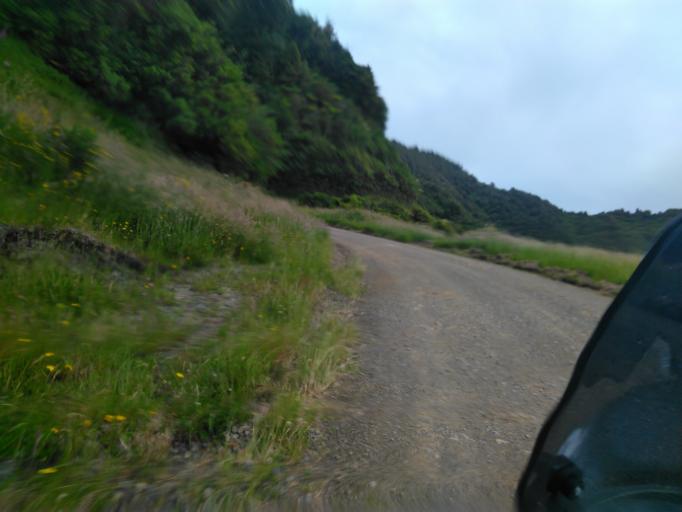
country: NZ
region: Bay of Plenty
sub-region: Opotiki District
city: Opotiki
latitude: -38.0953
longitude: 177.4857
